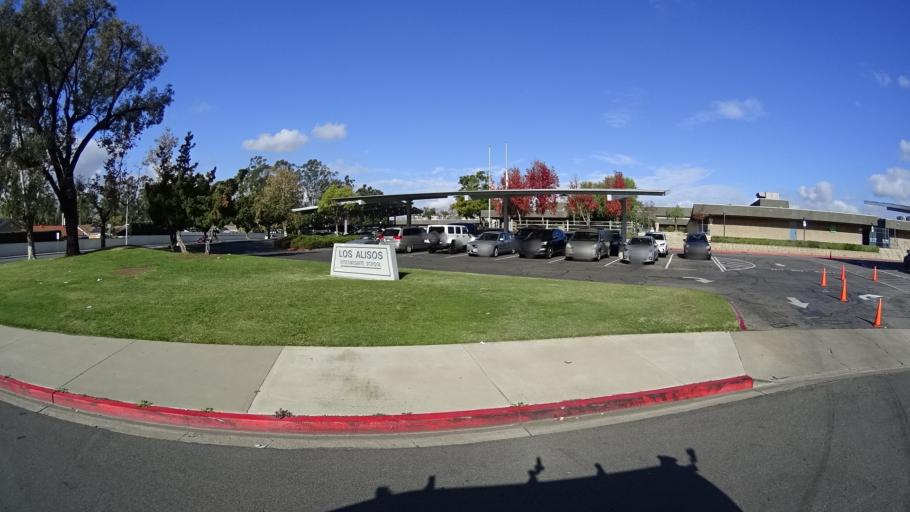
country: US
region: California
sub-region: Orange County
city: Laguna Hills
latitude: 33.6160
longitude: -117.6909
